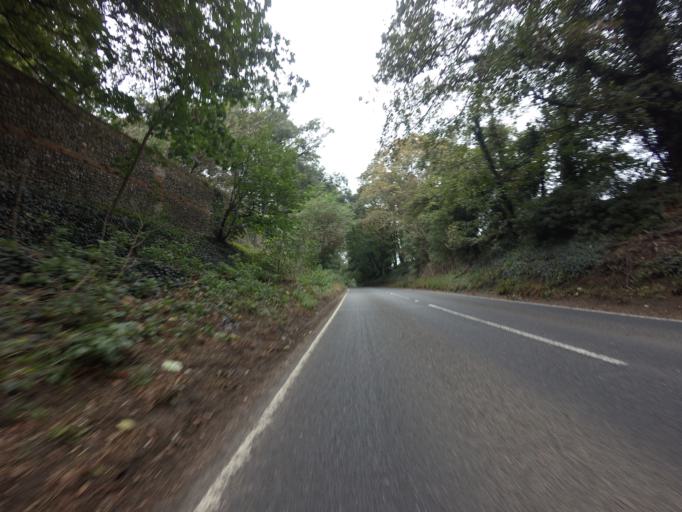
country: GB
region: England
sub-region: Essex
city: Saffron Walden
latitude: 52.0297
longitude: 0.2284
